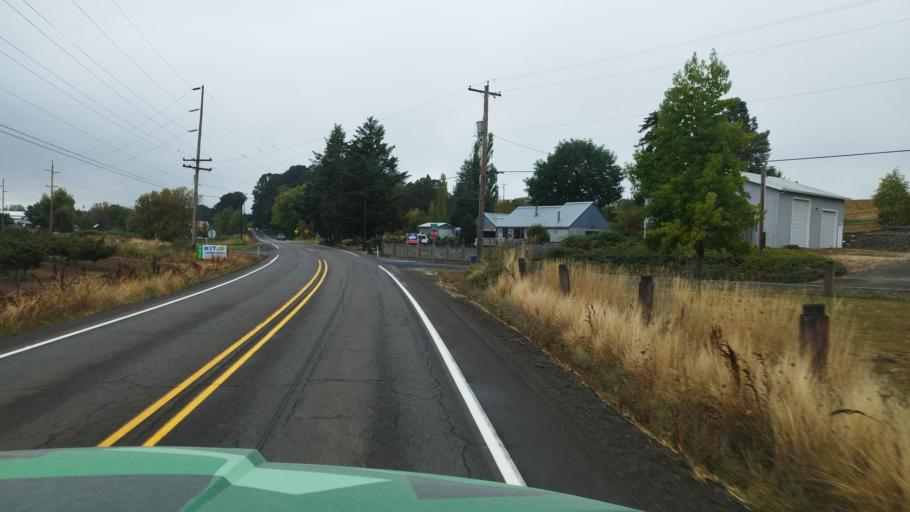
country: US
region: Oregon
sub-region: Yamhill County
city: Yamhill
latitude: 45.3508
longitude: -123.1747
